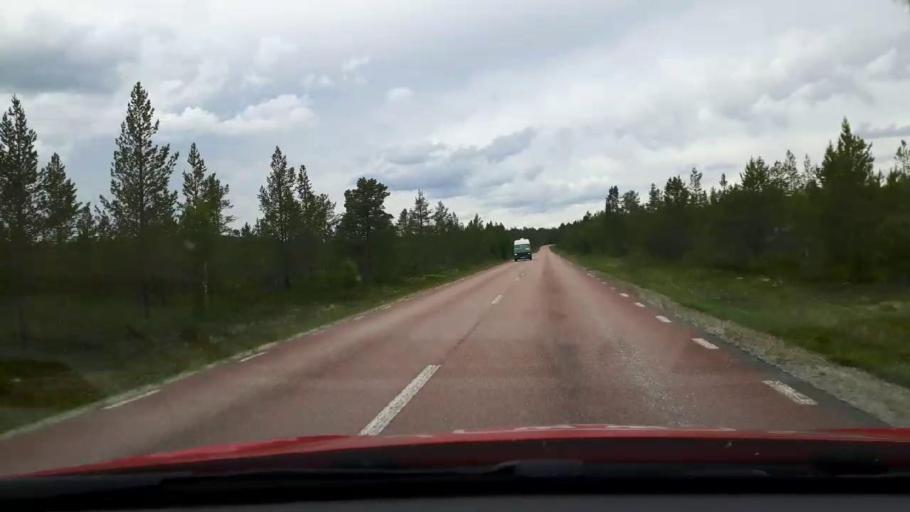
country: NO
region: Hedmark
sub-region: Engerdal
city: Engerdal
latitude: 62.4888
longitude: 12.6468
